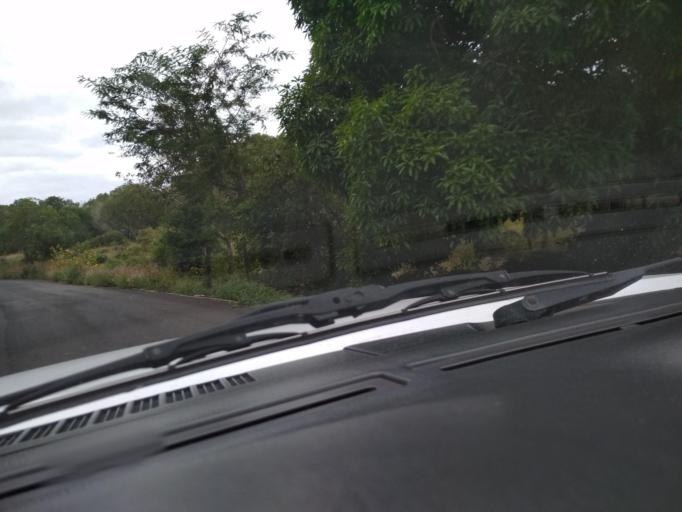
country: MX
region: Veracruz
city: Alto Lucero
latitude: 19.5946
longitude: -96.7862
